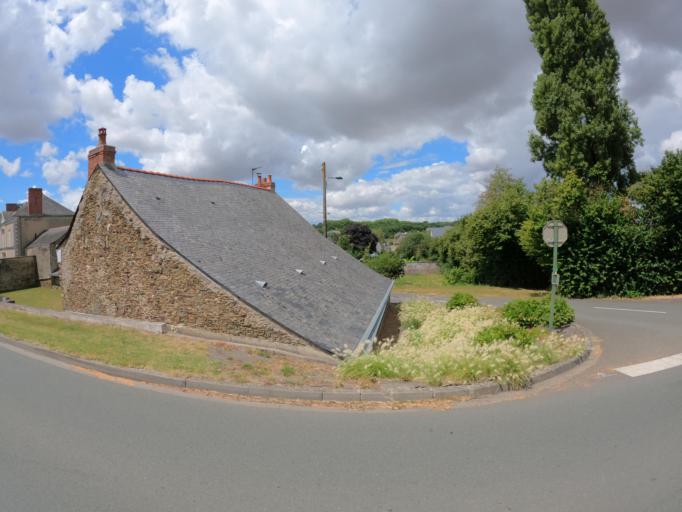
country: FR
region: Pays de la Loire
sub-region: Departement de Maine-et-Loire
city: Mire
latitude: 47.7561
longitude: -0.4941
